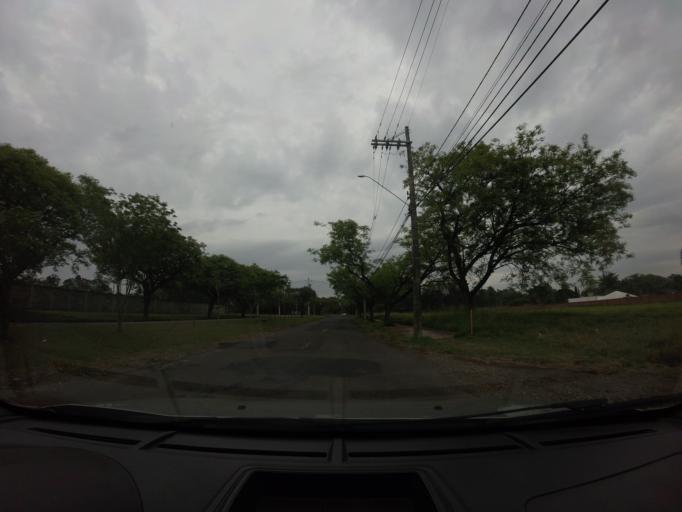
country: BR
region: Sao Paulo
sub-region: Piracicaba
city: Piracicaba
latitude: -22.7598
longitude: -47.5936
